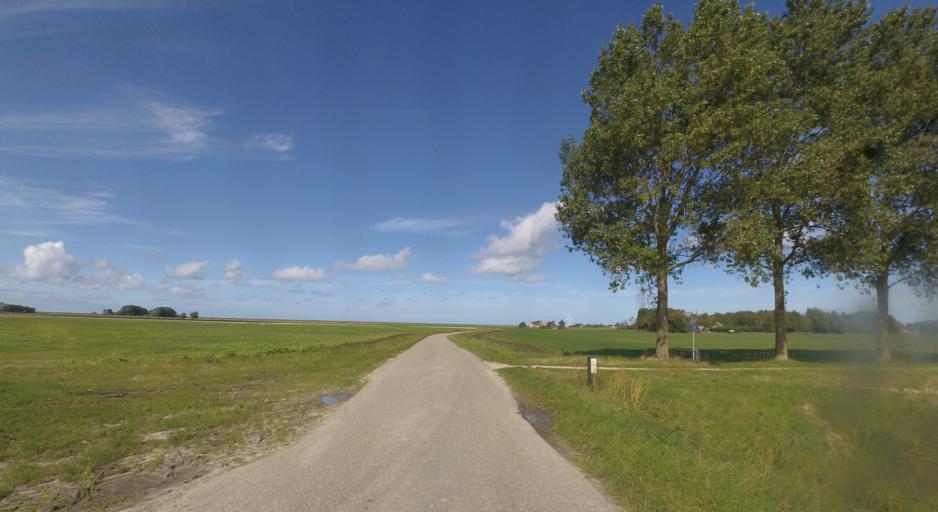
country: NL
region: Friesland
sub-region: Gemeente Dongeradeel
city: Holwerd
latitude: 53.3611
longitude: 5.8967
